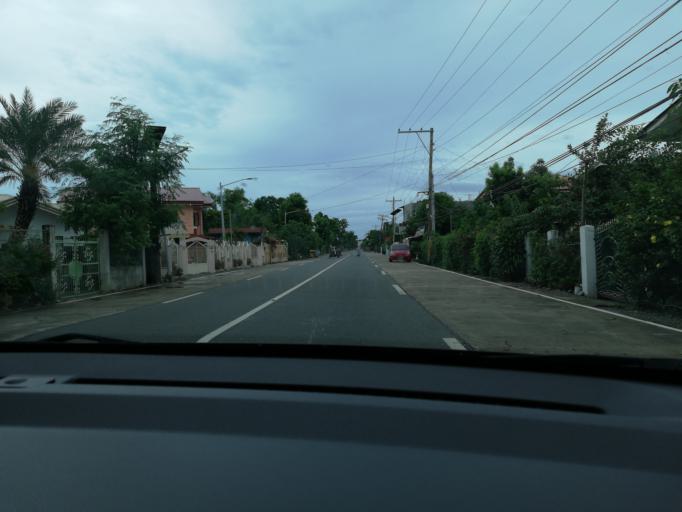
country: PH
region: Ilocos
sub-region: Province of Ilocos Sur
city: San Vicente
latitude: 17.5852
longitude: 120.3703
